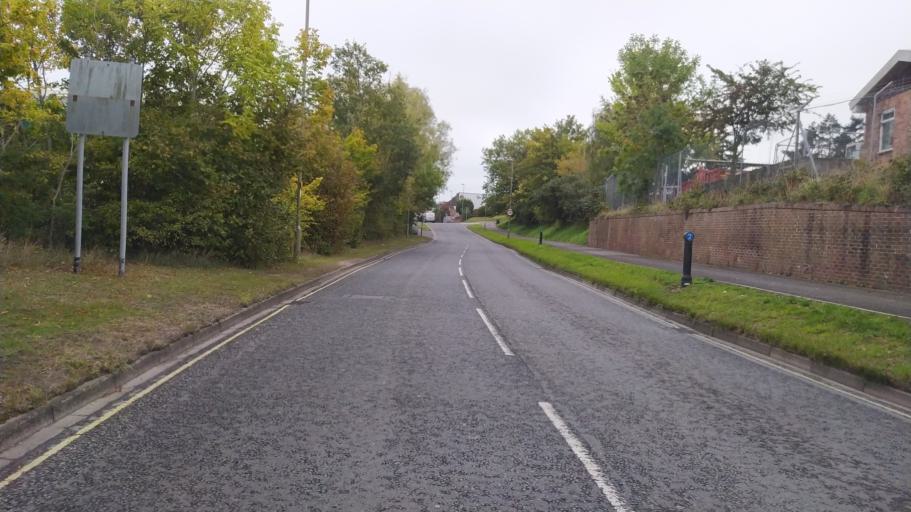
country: GB
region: England
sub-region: Hampshire
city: Lymington
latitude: 50.7647
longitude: -1.5427
